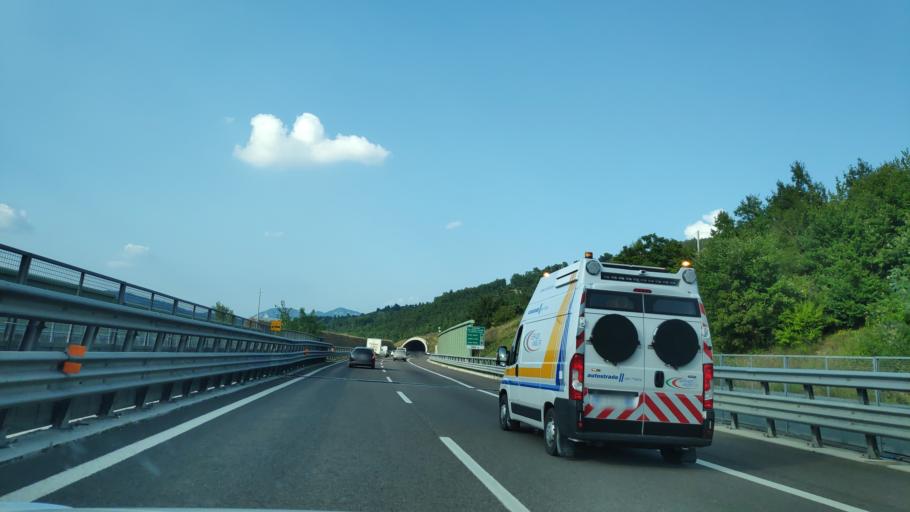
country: IT
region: Emilia-Romagna
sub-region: Provincia di Bologna
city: Grizzana
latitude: 44.2367
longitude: 11.1856
